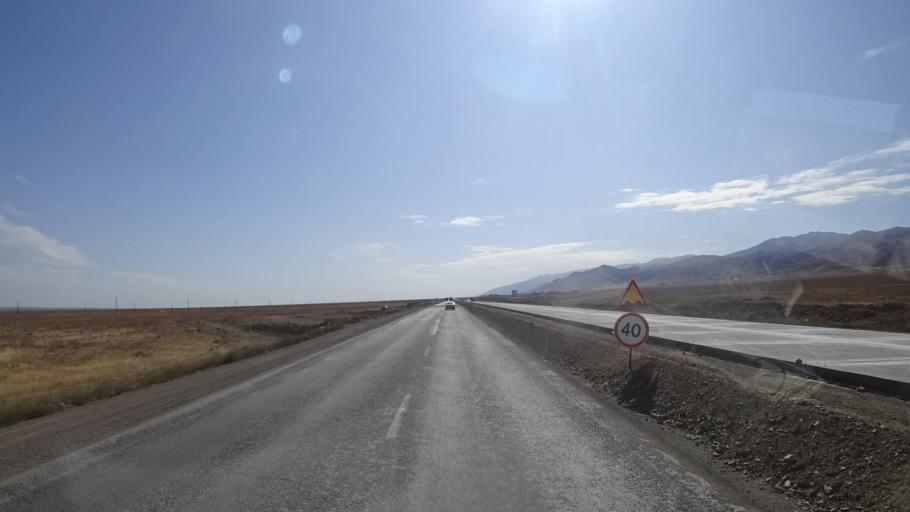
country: KG
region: Chuy
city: Ivanovka
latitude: 43.3974
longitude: 75.1226
